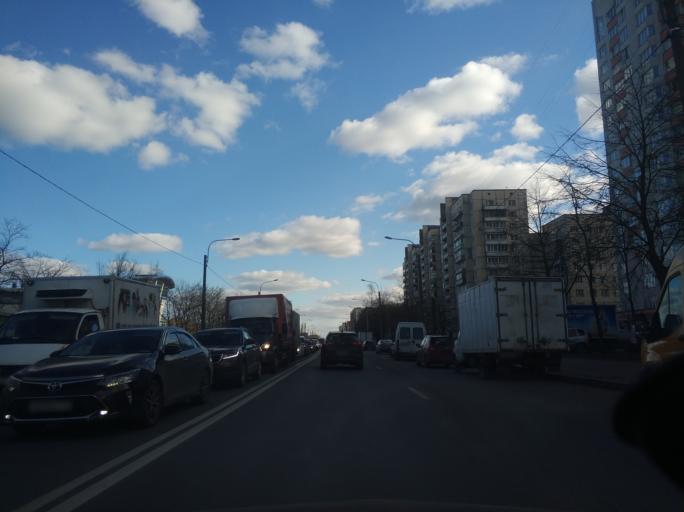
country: RU
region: St.-Petersburg
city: Krasnogvargeisky
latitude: 59.9597
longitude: 30.4910
